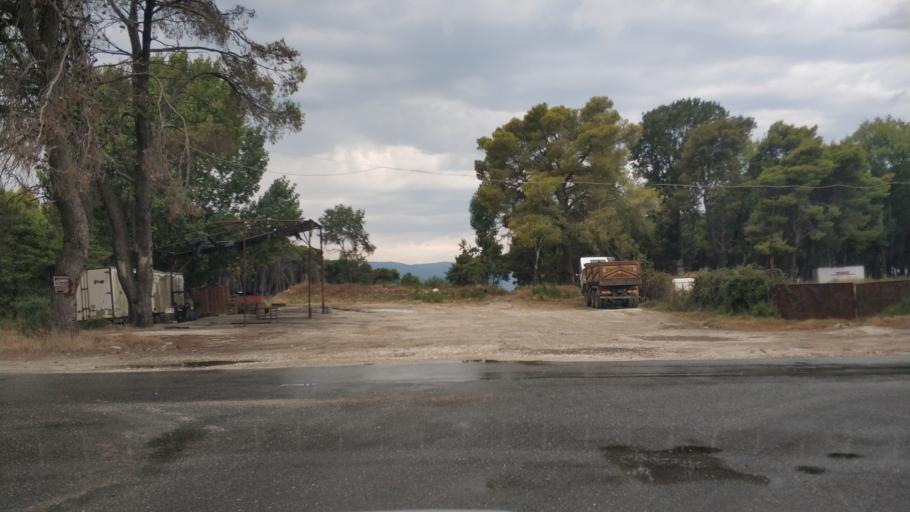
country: AL
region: Vlore
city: Vlore
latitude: 40.4713
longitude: 19.4584
